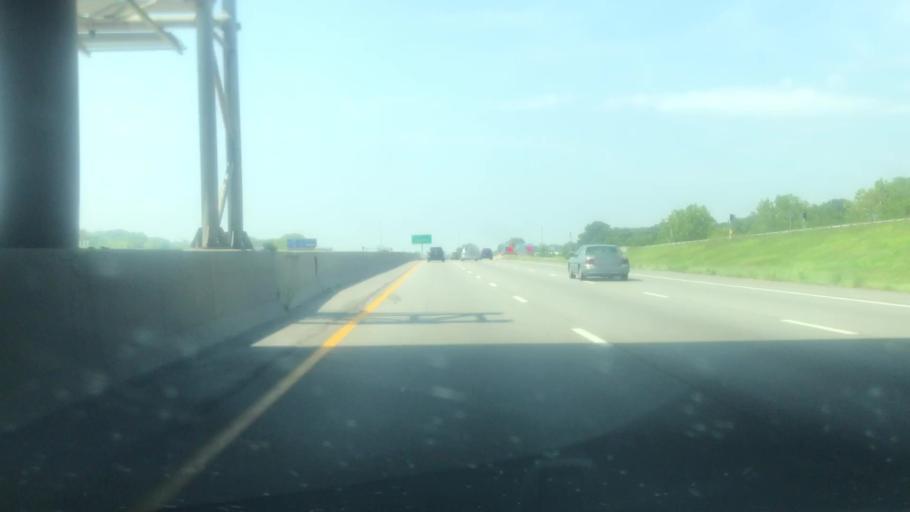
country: US
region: Kansas
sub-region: Johnson County
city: Roeland Park
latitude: 39.0478
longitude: -94.6463
